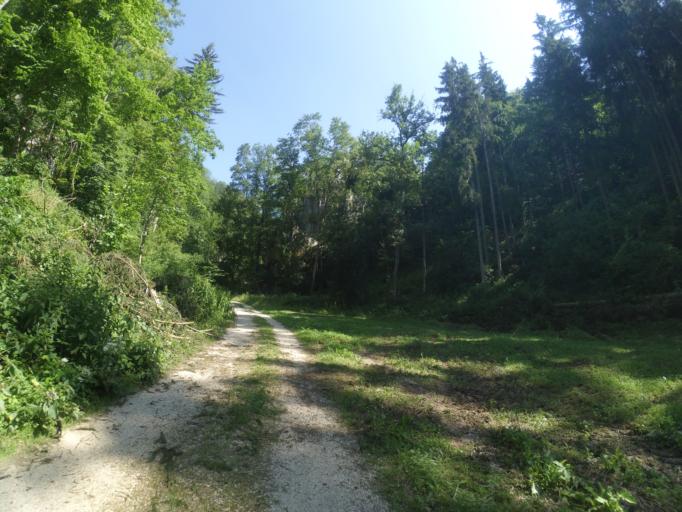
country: DE
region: Baden-Wuerttemberg
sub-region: Tuebingen Region
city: Dornstadt
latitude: 48.4456
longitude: 9.8996
